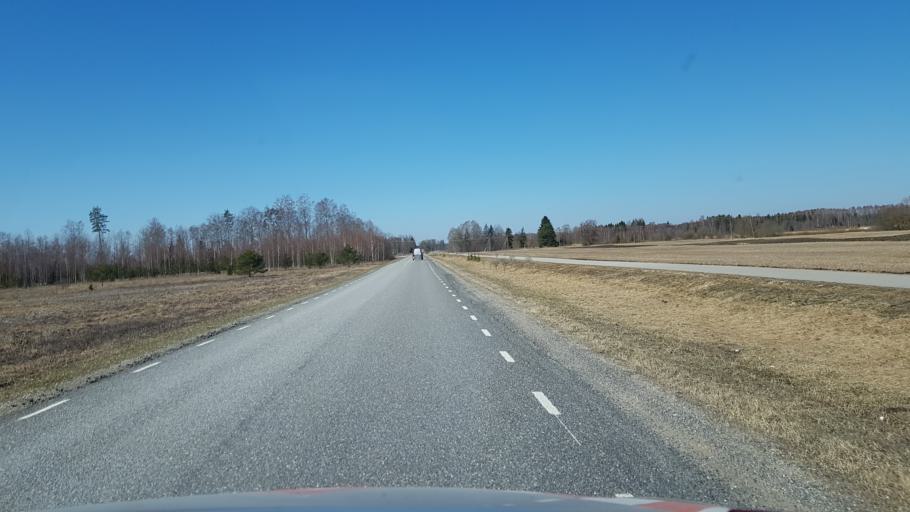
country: EE
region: Laeaene-Virumaa
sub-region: Rakke vald
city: Rakke
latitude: 58.9953
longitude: 26.2168
